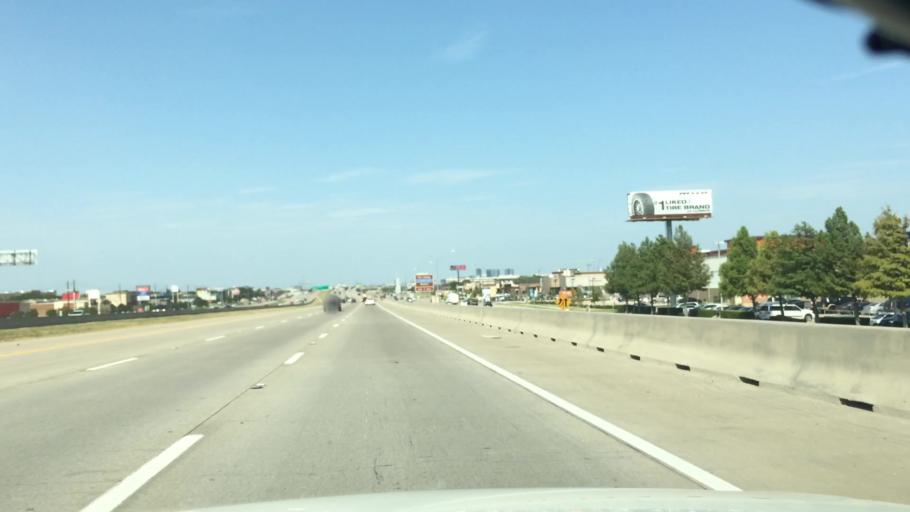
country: US
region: Texas
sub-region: Denton County
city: The Colony
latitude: 33.0673
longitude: -96.8850
